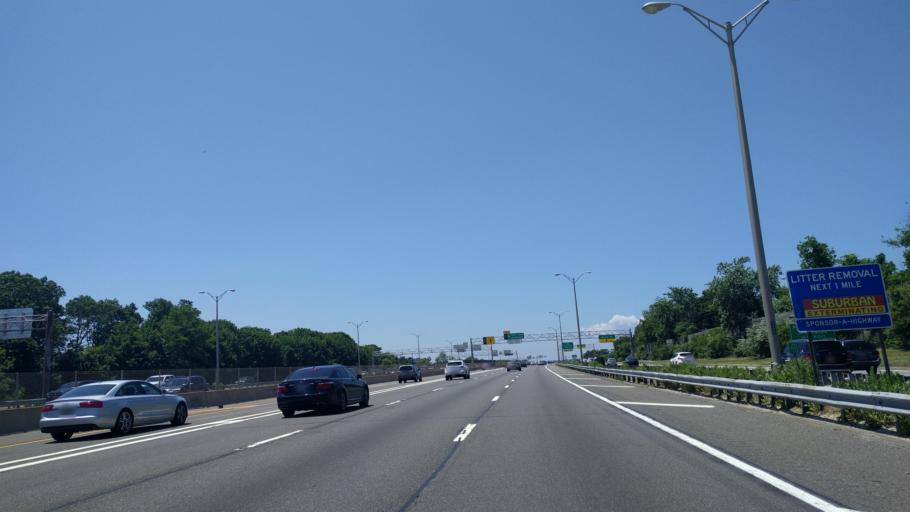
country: US
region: New York
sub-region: Suffolk County
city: Brentwood
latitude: 40.8049
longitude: -73.2608
